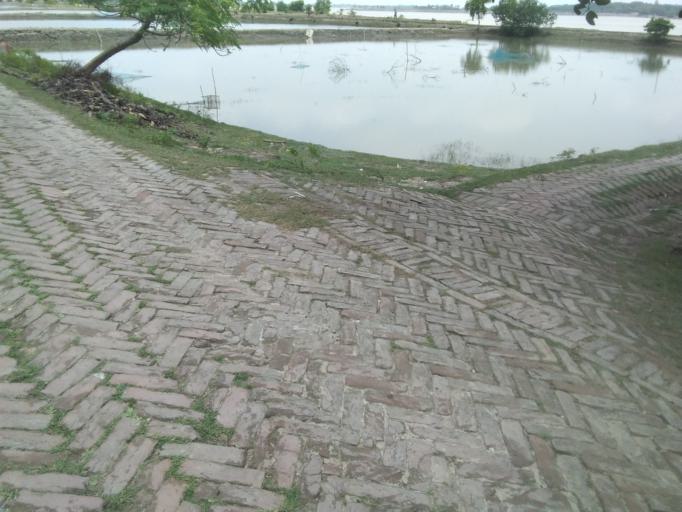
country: BD
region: Khulna
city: Phultala
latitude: 22.6421
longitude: 89.4193
